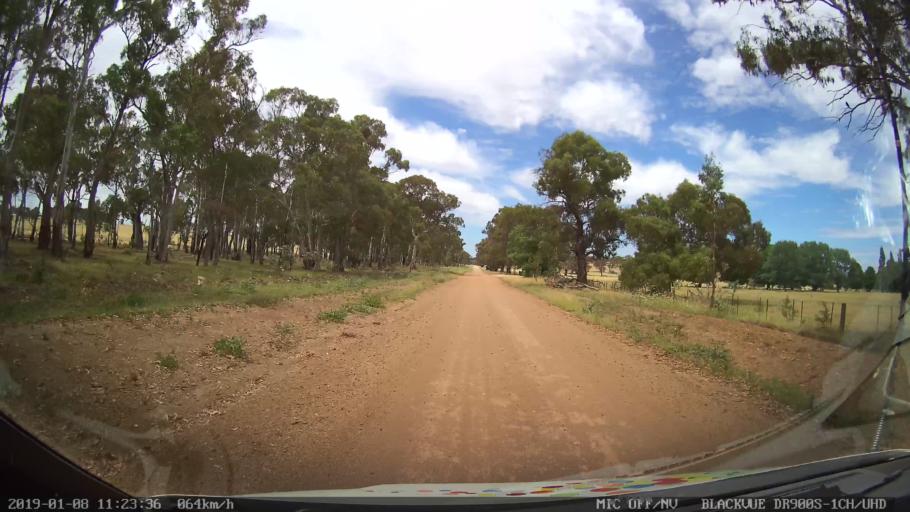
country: AU
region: New South Wales
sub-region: Guyra
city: Guyra
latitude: -30.2568
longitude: 151.5588
